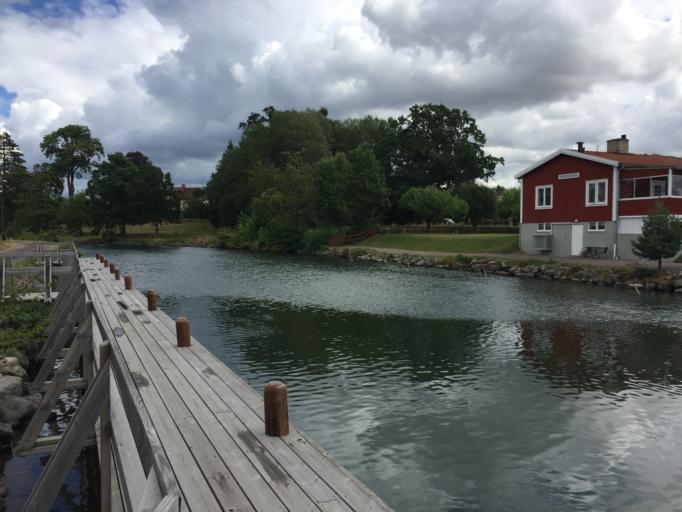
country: SE
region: OEstergoetland
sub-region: Motala Kommun
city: Borensberg
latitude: 58.5600
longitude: 15.2839
